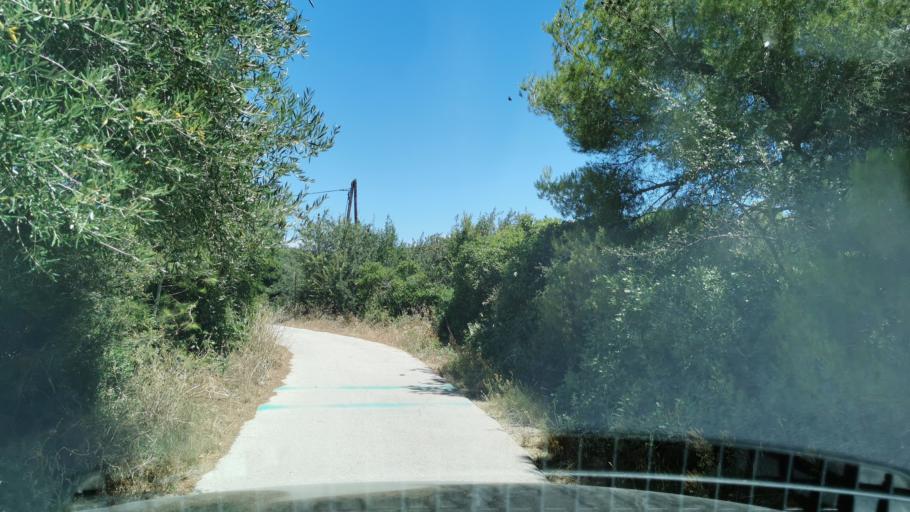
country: FR
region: Languedoc-Roussillon
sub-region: Departement de l'Aude
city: Peyriac-de-Mer
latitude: 43.1106
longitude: 2.9639
